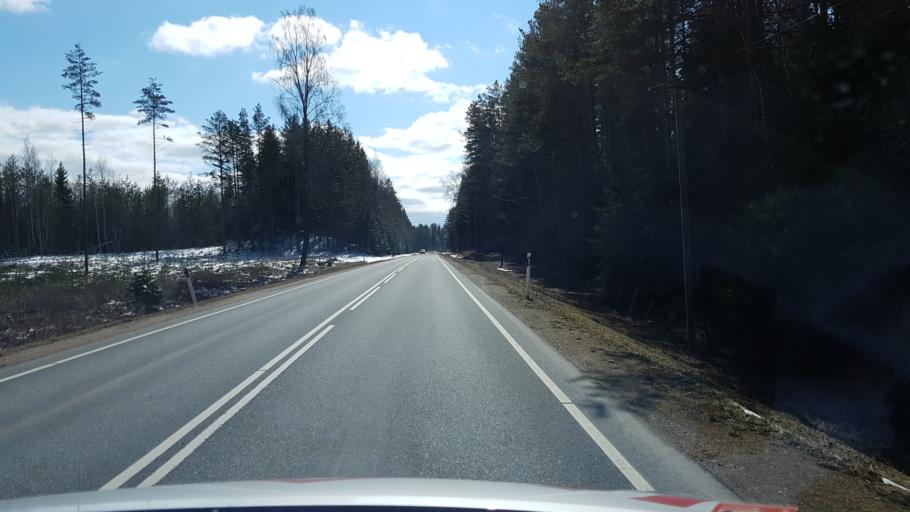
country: EE
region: Laeaene-Virumaa
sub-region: Kadrina vald
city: Kadrina
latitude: 59.3989
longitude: 26.0130
